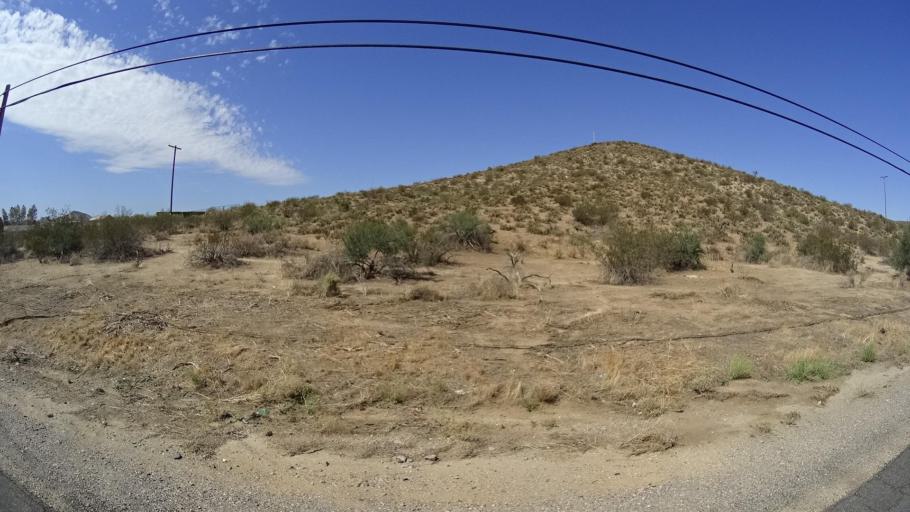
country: MX
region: Baja California
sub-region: Tecate
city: Cereso del Hongo
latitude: 32.6183
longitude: -116.1638
